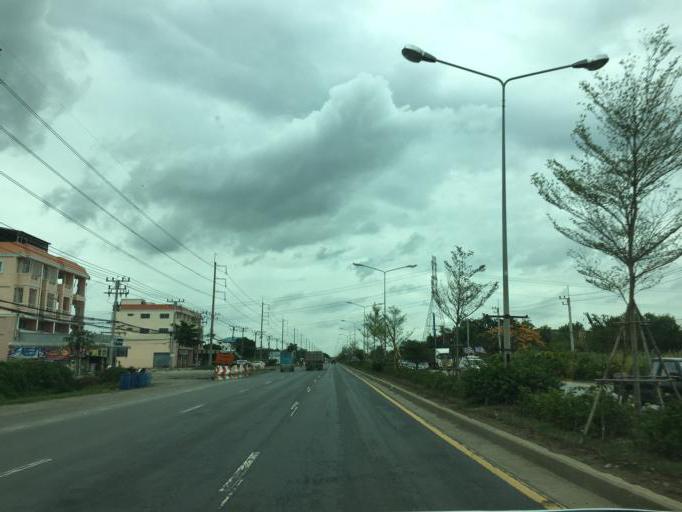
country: TH
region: Phra Nakhon Si Ayutthaya
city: Wang Noi
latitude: 14.2612
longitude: 100.6932
